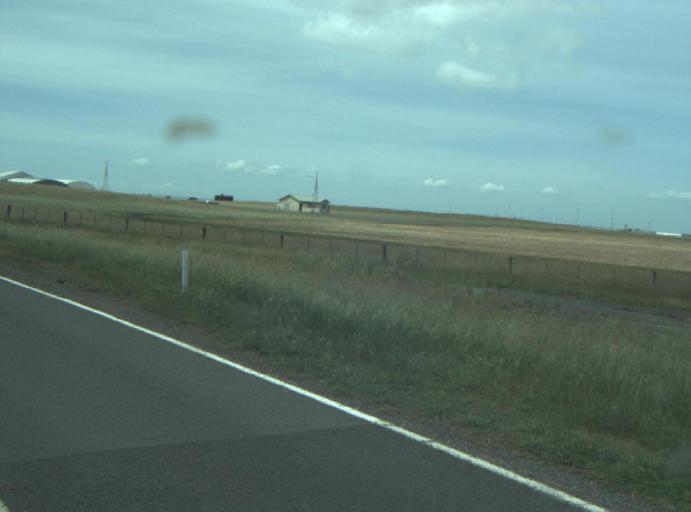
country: AU
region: Victoria
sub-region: Wyndham
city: Little River
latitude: -38.0163
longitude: 144.4693
